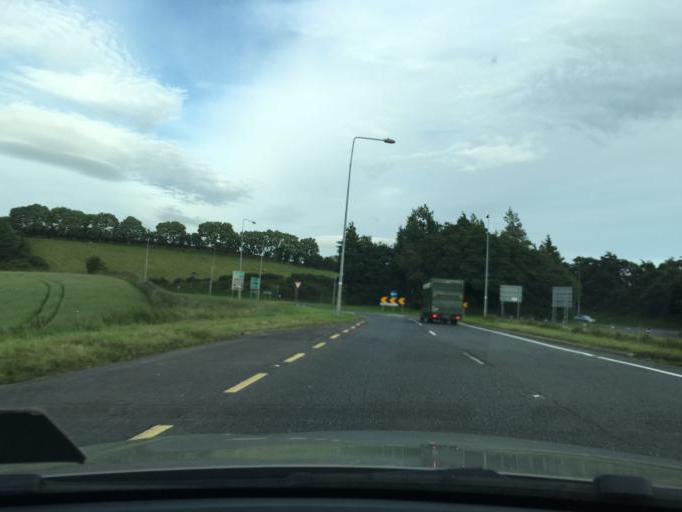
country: IE
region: Ulster
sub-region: County Donegal
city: Raphoe
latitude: 54.9446
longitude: -7.6377
